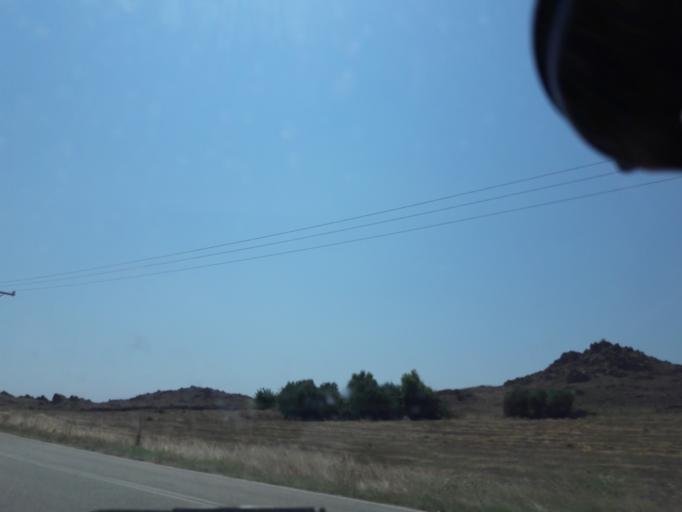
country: GR
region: North Aegean
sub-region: Nomos Lesvou
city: Myrina
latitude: 39.8584
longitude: 25.1427
